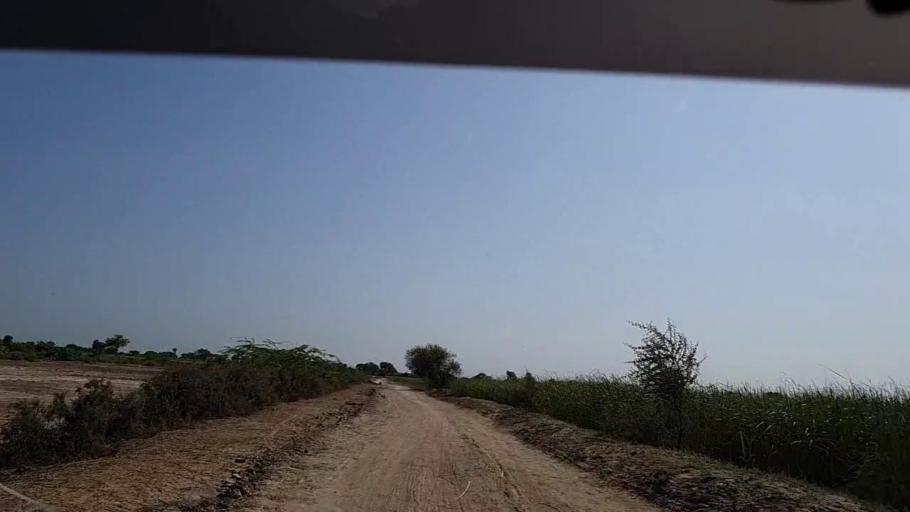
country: PK
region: Sindh
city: Badin
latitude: 24.6230
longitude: 68.7816
